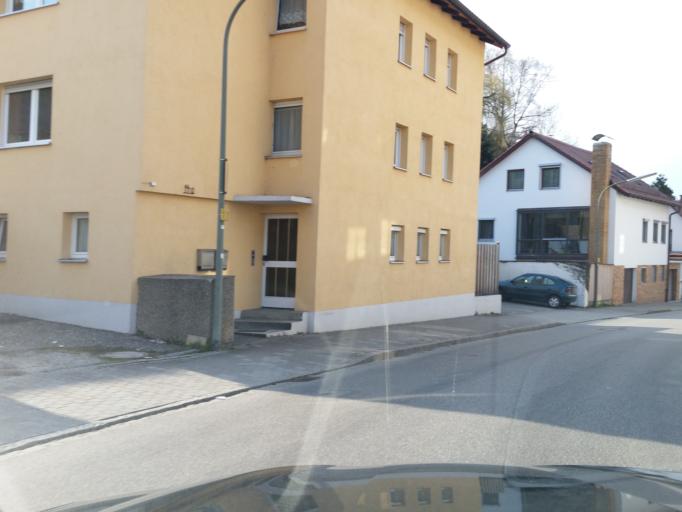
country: DE
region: Bavaria
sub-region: Lower Bavaria
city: Landshut
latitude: 48.5359
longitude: 12.1684
